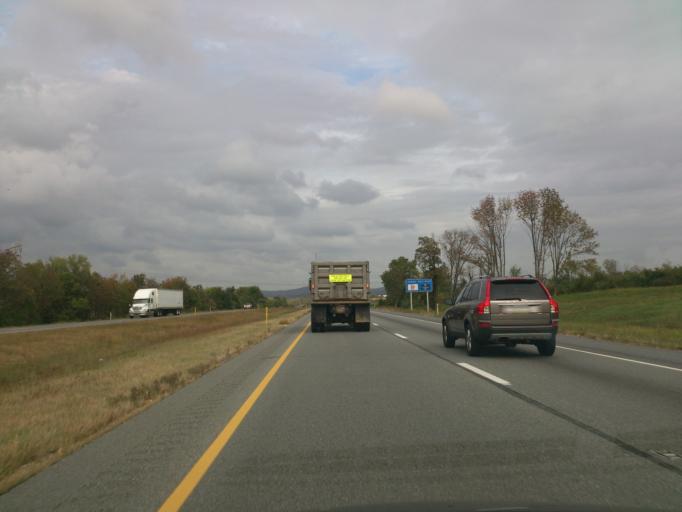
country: US
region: Pennsylvania
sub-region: Lancaster County
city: Reamstown
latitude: 40.2113
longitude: -76.1034
